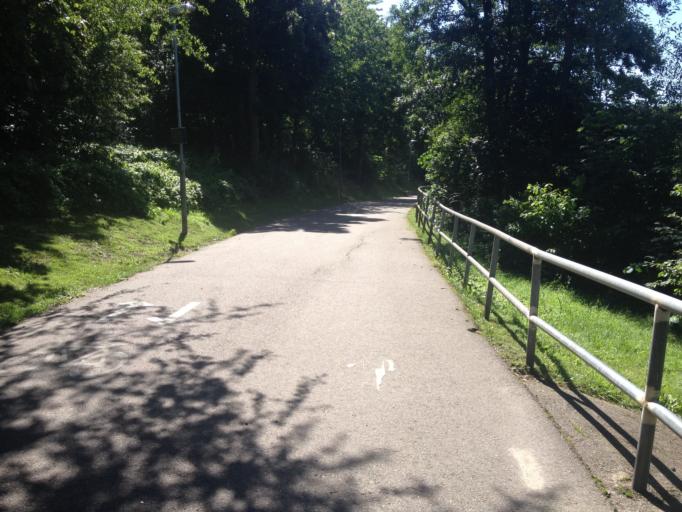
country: SE
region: Skane
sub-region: Angelholms Kommun
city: AEngelholm
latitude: 56.2410
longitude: 12.8659
